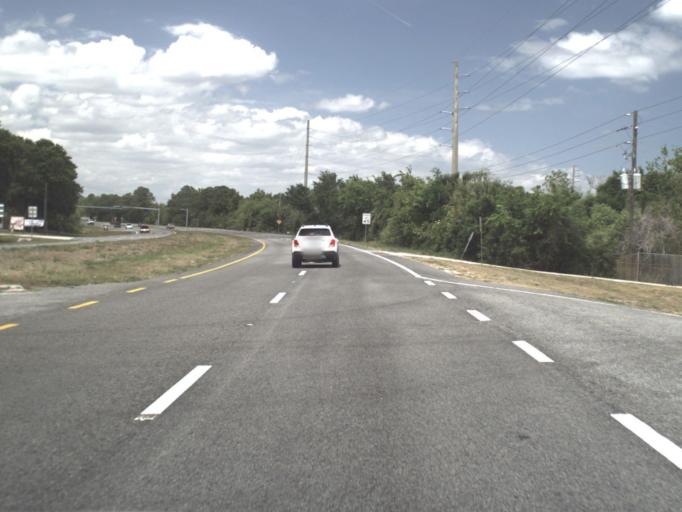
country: US
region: Florida
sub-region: Brevard County
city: Titusville
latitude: 28.5510
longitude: -80.8371
